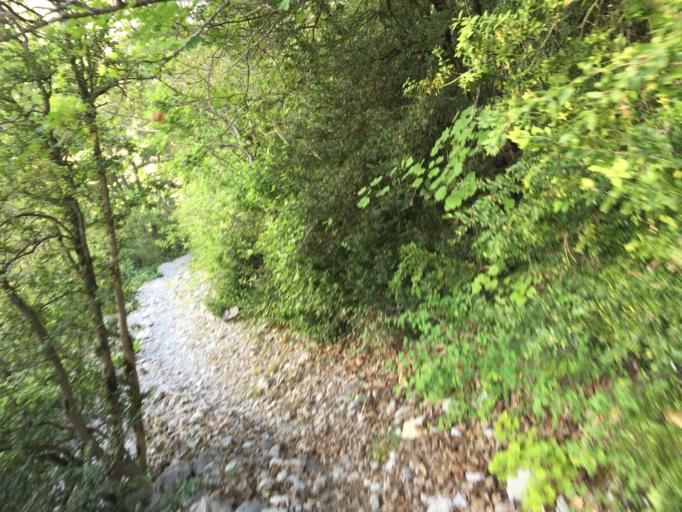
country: FR
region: Provence-Alpes-Cote d'Azur
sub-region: Departement des Alpes-de-Haute-Provence
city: Digne-les-Bains
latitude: 43.9473
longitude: 6.2459
